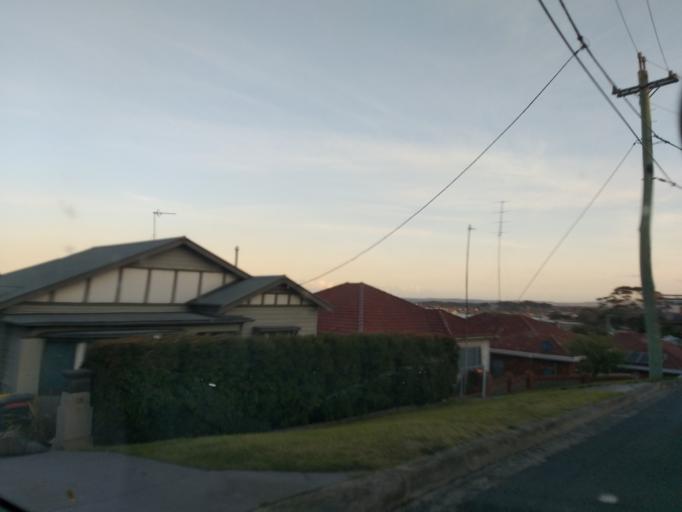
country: AU
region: New South Wales
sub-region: Wollongong
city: Lake Heights
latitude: -34.4825
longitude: 150.8823
